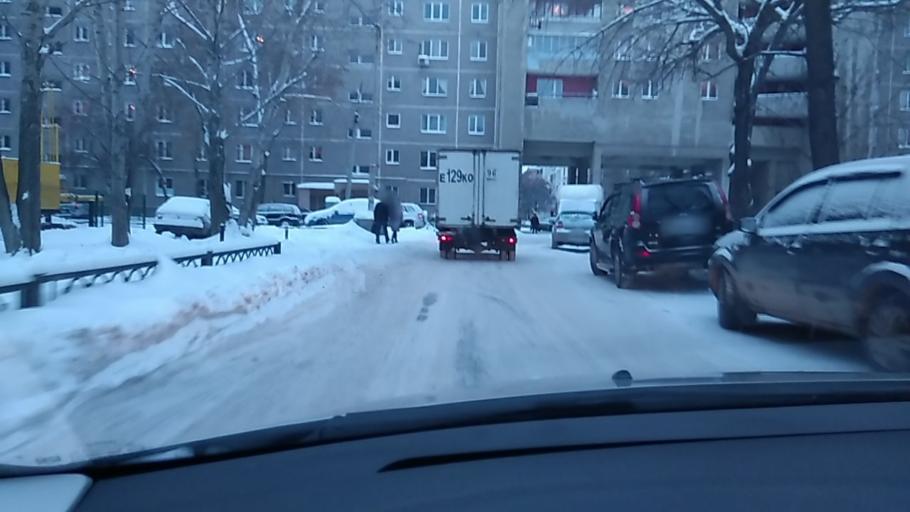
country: RU
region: Sverdlovsk
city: Yekaterinburg
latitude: 56.8926
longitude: 60.5960
